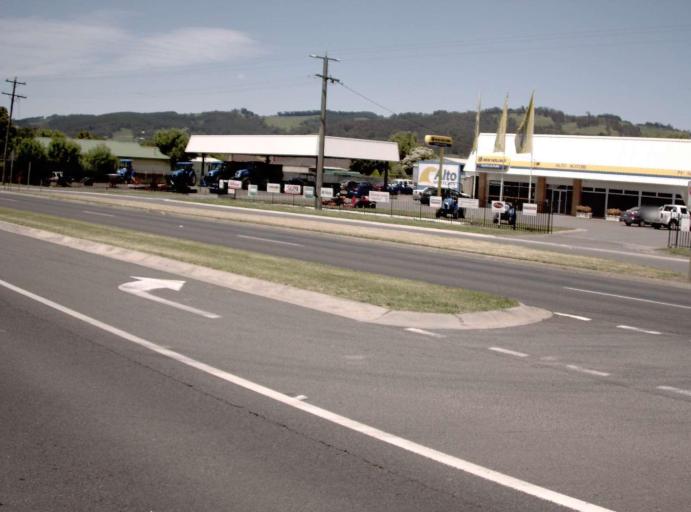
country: AU
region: Victoria
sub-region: Latrobe
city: Moe
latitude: -38.2090
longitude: 146.1446
